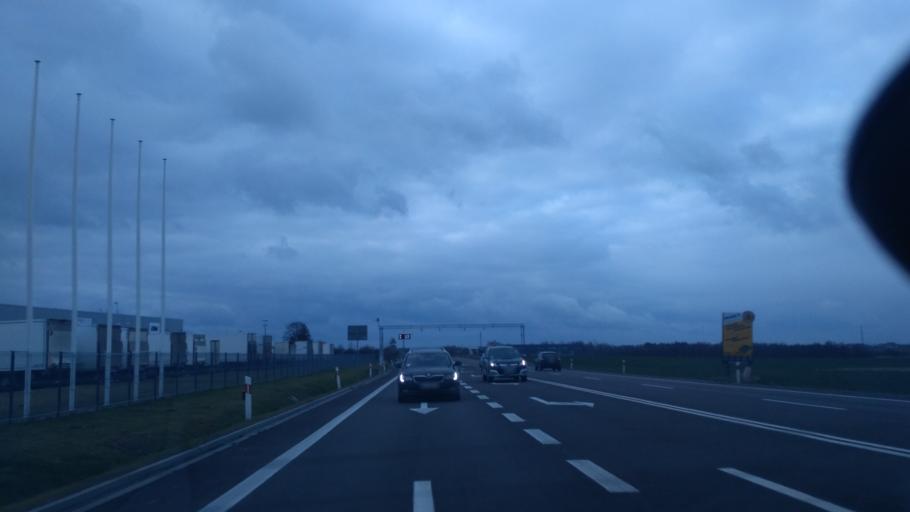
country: PL
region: Subcarpathian Voivodeship
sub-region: Powiat rzeszowski
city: Krasne
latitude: 50.0436
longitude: 22.1189
